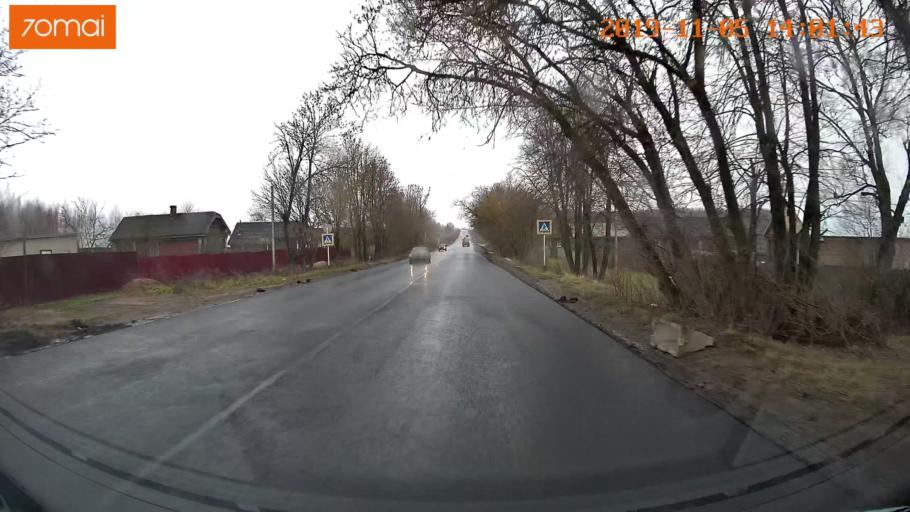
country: RU
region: Ivanovo
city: Kitovo
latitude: 57.0071
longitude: 41.2257
